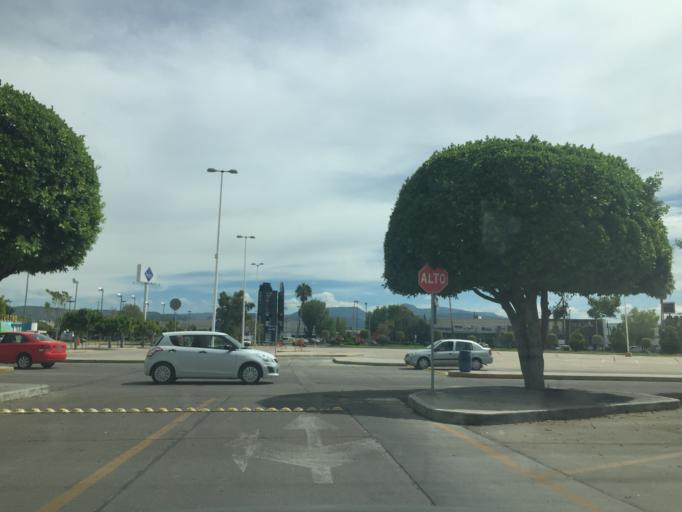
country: MX
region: Guanajuato
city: Leon
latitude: 21.1581
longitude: -101.6933
